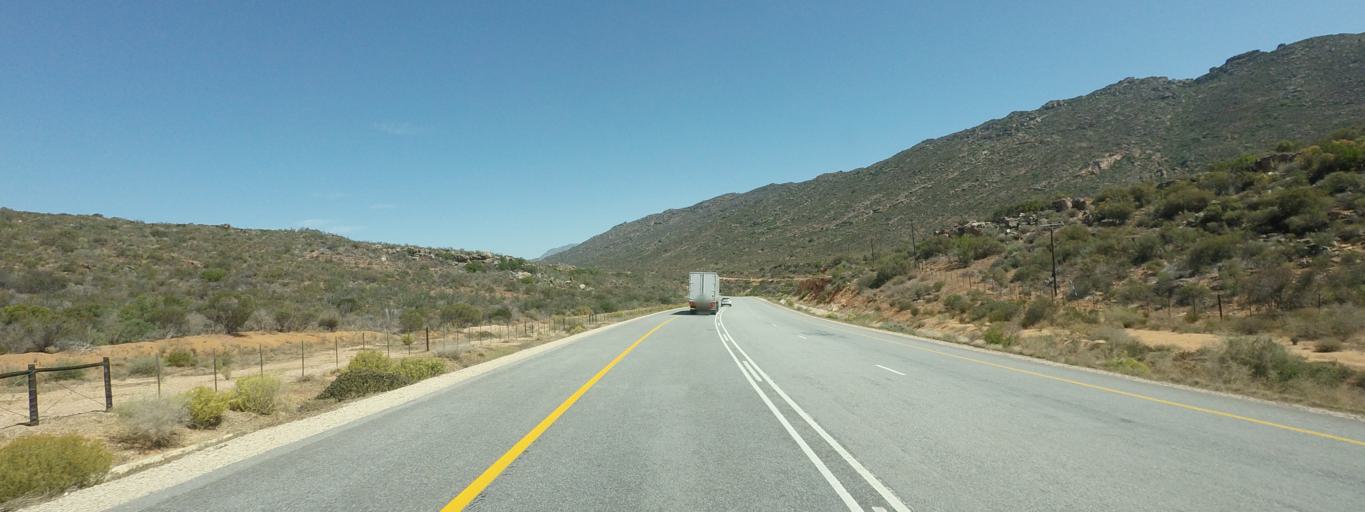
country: ZA
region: Western Cape
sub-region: West Coast District Municipality
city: Clanwilliam
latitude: -32.3350
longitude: 18.9249
